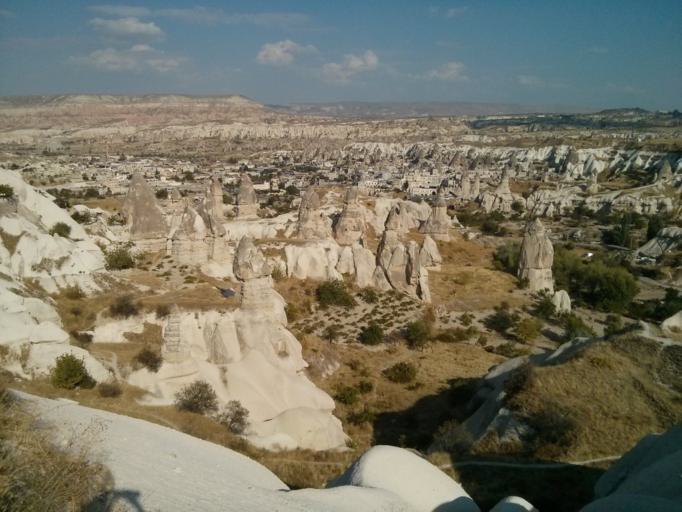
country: TR
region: Nevsehir
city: Goereme
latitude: 38.6446
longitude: 34.8340
